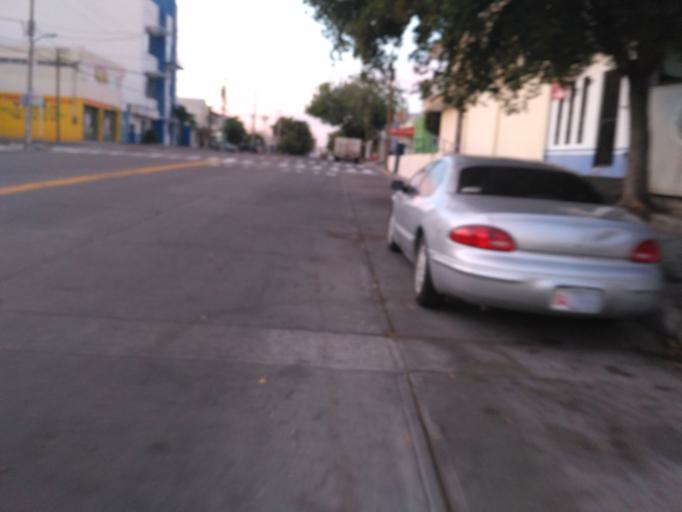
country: MX
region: Sinaloa
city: Culiacan
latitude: 24.8015
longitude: -107.4040
